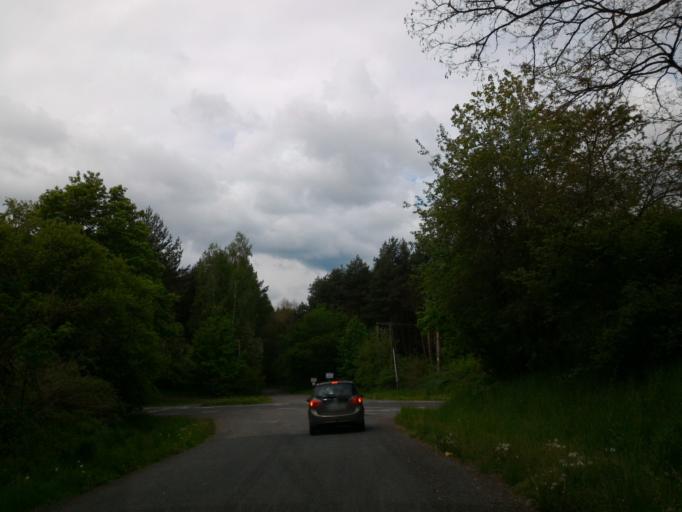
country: CZ
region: Vysocina
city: Ledec nad Sazavou
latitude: 49.6234
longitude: 15.2562
